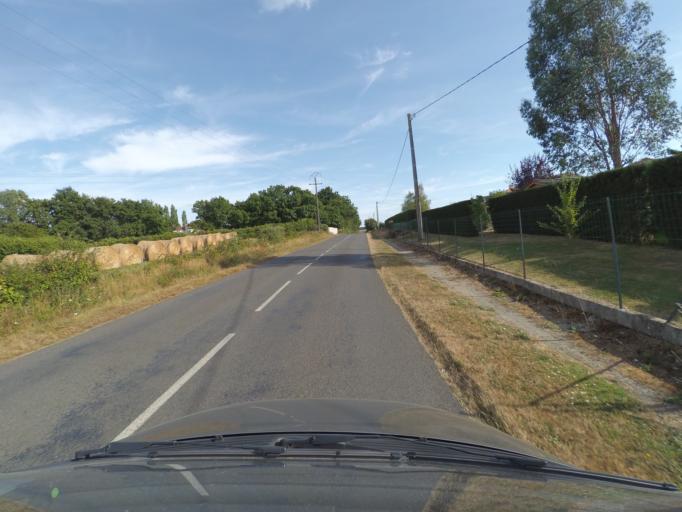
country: FR
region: Pays de la Loire
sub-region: Departement de la Loire-Atlantique
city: Montbert
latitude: 47.0529
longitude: -1.4844
